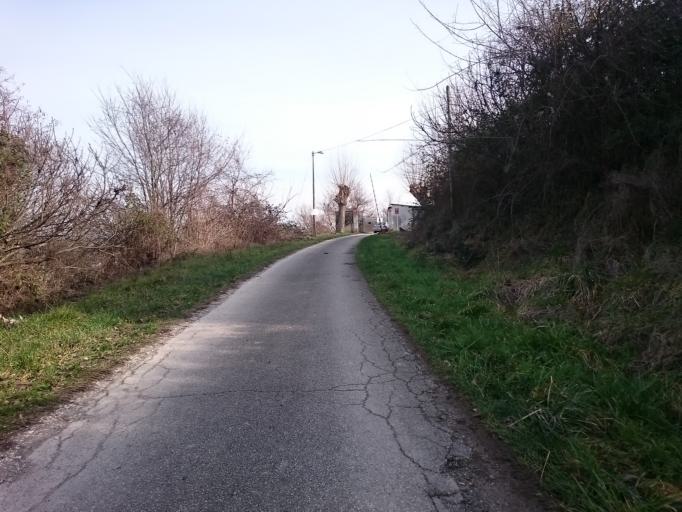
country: IT
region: Lombardy
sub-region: Provincia di Mantova
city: Ponti sul Mincio
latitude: 45.4240
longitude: 10.6920
